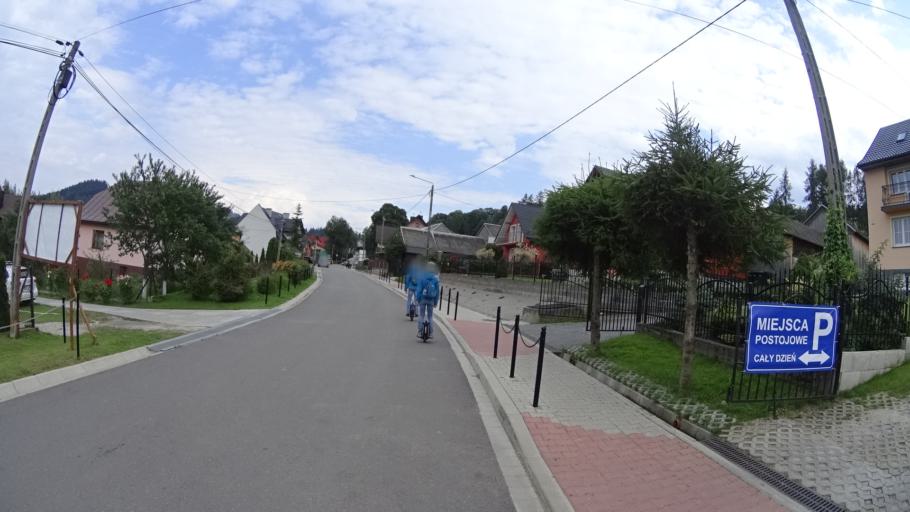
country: PL
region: Lesser Poland Voivodeship
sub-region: Powiat nowotarski
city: Niedzica
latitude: 49.4237
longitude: 20.3115
